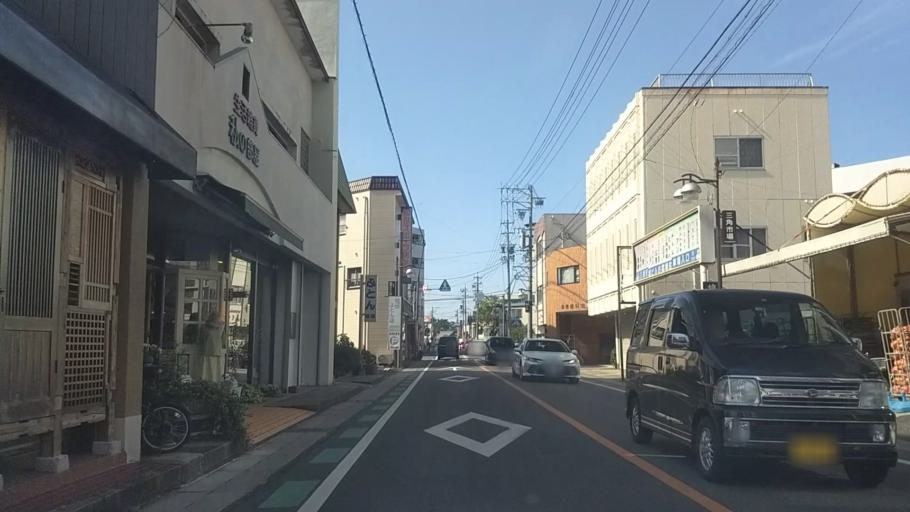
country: JP
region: Aichi
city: Anjo
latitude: 34.9867
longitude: 137.0840
